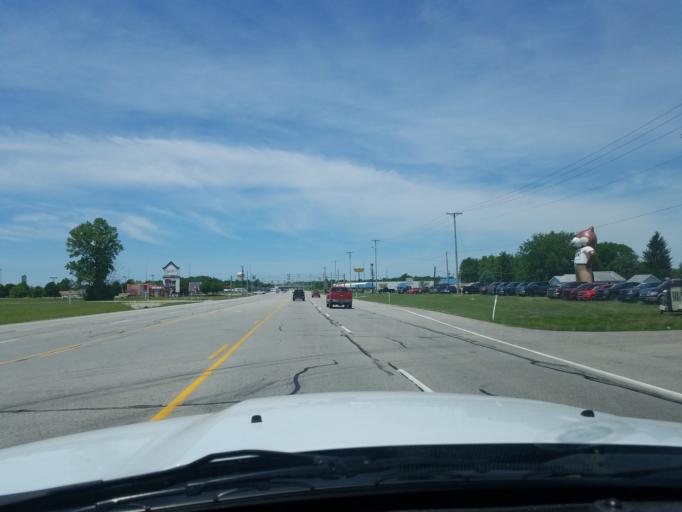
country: US
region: Indiana
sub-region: Delaware County
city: Daleville
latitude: 40.1136
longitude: -85.5599
